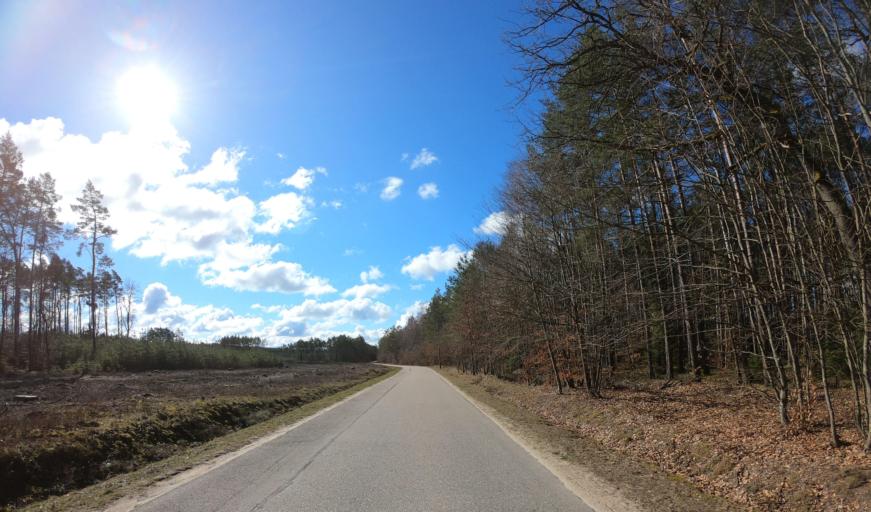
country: PL
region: West Pomeranian Voivodeship
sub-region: Powiat drawski
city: Zlocieniec
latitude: 53.4959
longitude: 15.9933
